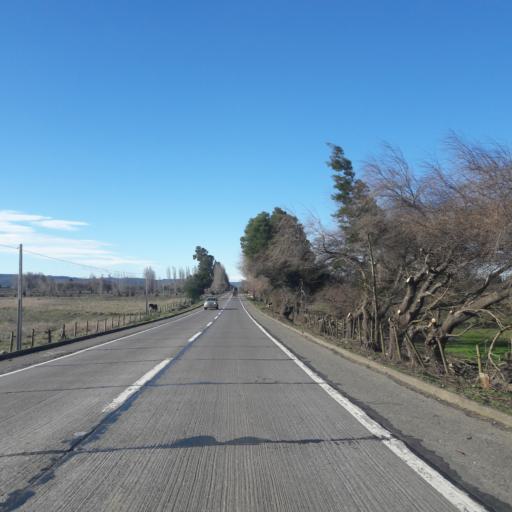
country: CL
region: Araucania
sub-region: Provincia de Malleco
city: Angol
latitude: -37.7681
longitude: -72.5567
